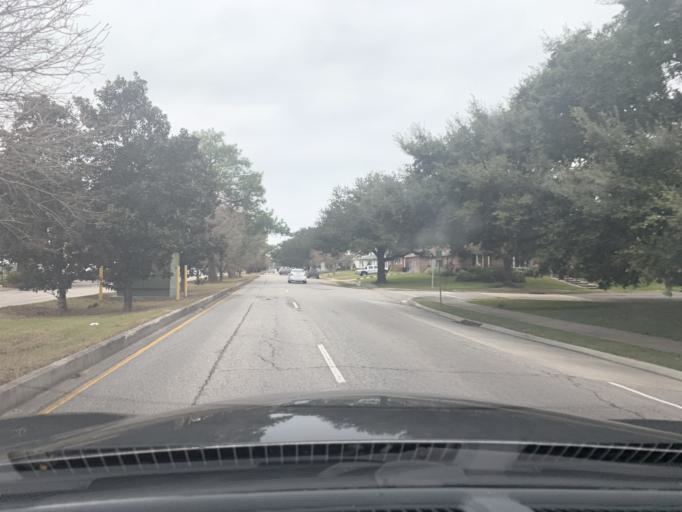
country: US
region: Louisiana
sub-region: Jefferson Parish
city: Metairie
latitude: 30.0197
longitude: -90.1071
